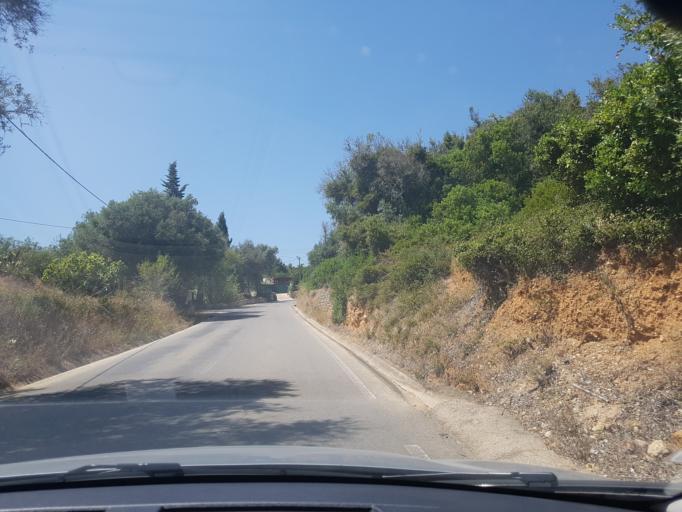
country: PT
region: Faro
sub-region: Lagoa
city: Carvoeiro
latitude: 37.1027
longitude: -8.4283
